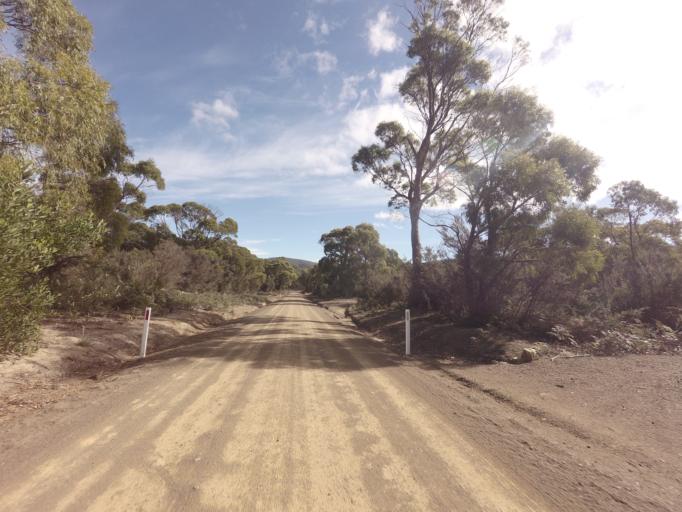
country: AU
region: Tasmania
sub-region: Clarence
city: Sandford
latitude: -43.0861
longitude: 147.6920
